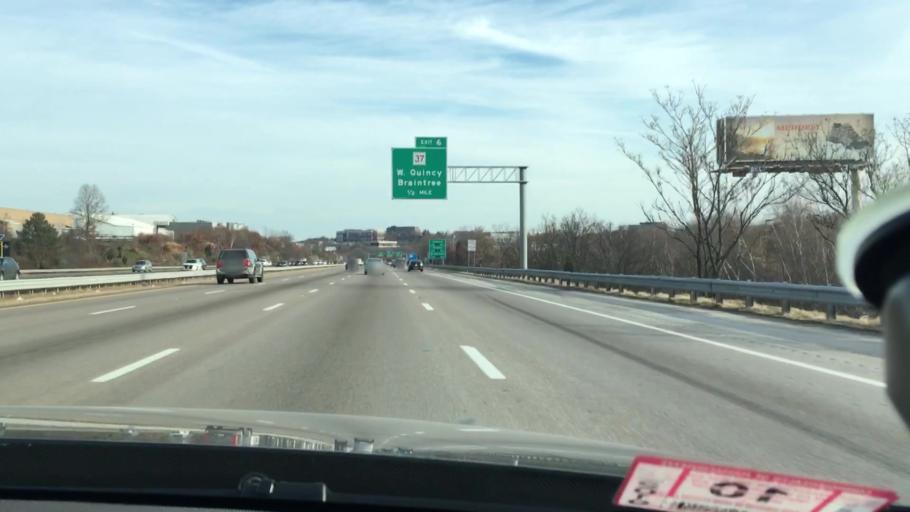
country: US
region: Massachusetts
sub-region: Norfolk County
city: Braintree
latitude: 42.2147
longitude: -71.0410
